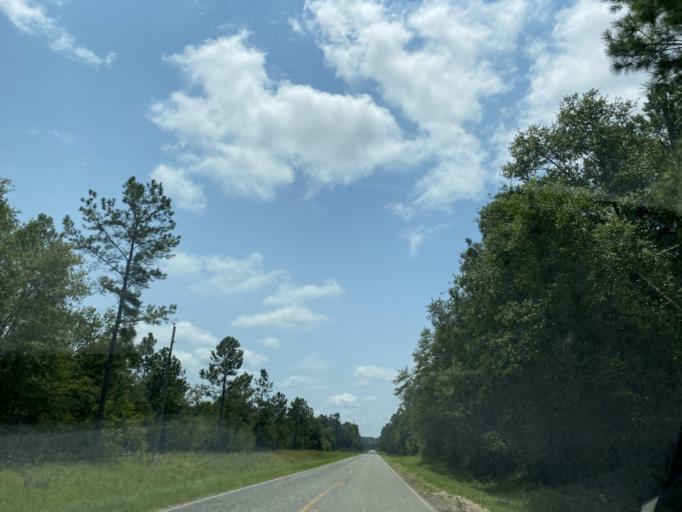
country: US
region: Georgia
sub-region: Telfair County
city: Lumber City
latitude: 31.9782
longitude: -82.7029
